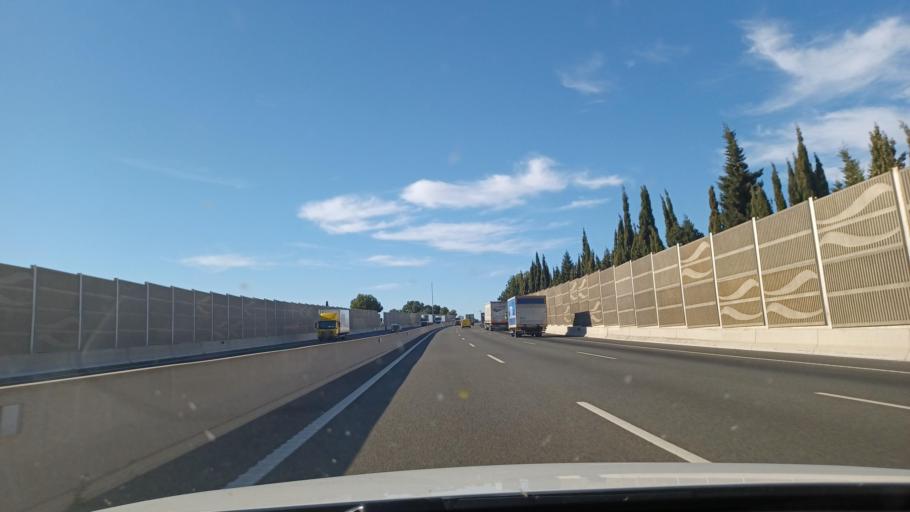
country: ES
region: Valencia
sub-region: Provincia de Valencia
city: Picassent
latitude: 39.3851
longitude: -0.4734
